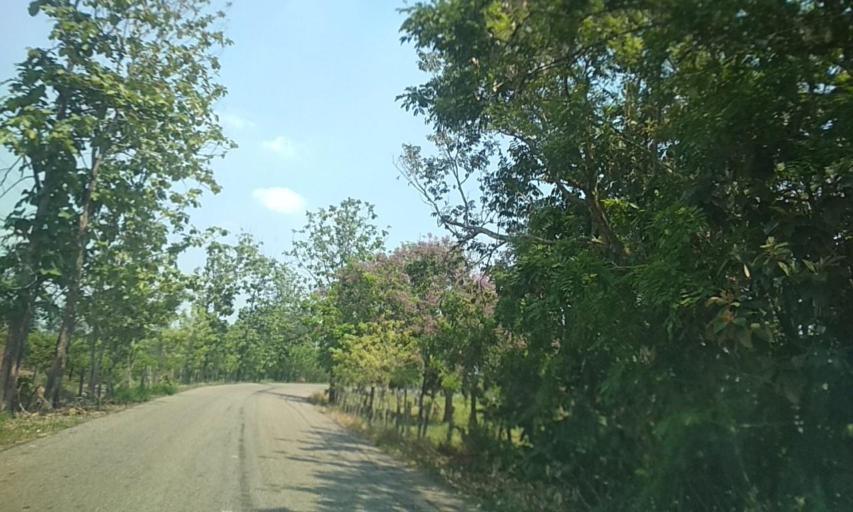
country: MX
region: Tabasco
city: Huimanguillo
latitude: 17.8188
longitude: -93.4993
